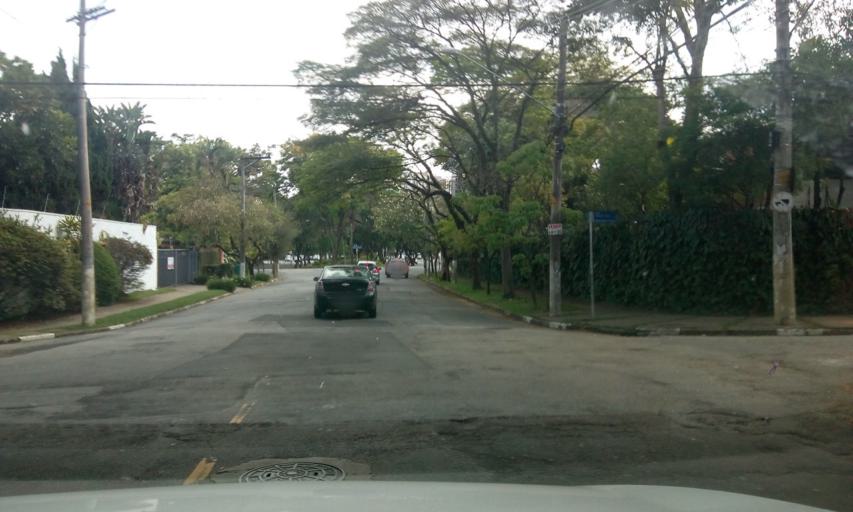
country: BR
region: Sao Paulo
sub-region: Sao Paulo
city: Sao Paulo
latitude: -23.5463
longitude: -46.7142
